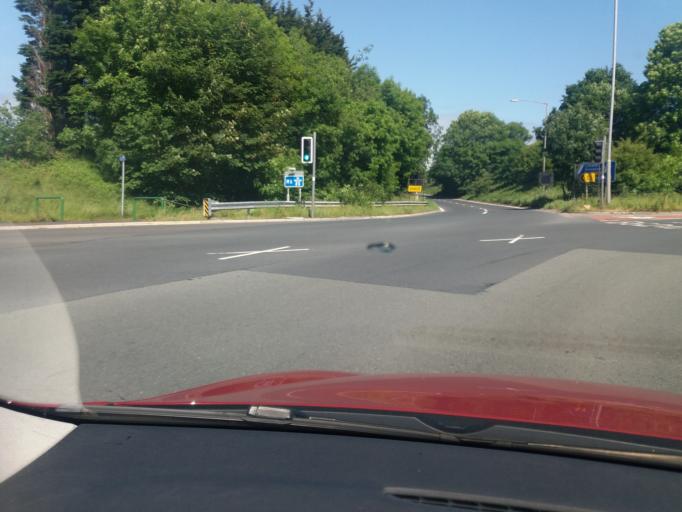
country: GB
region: England
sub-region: Lancashire
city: Preston
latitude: 53.8012
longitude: -2.7167
